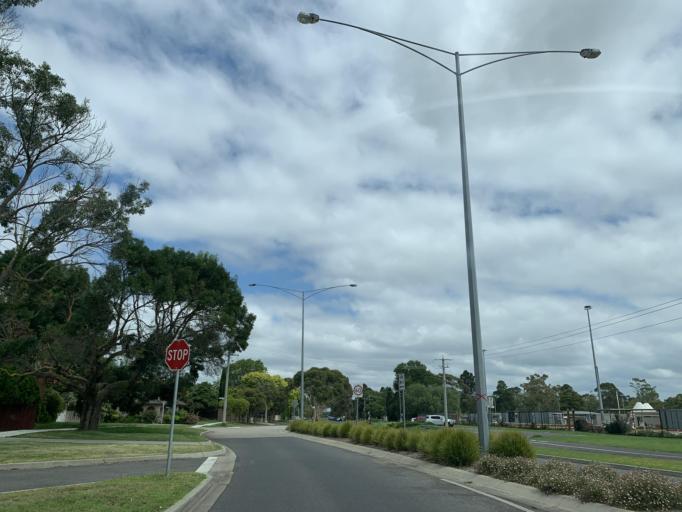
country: AU
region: Victoria
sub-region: Wellington
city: Sale
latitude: -38.1112
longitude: 147.0813
